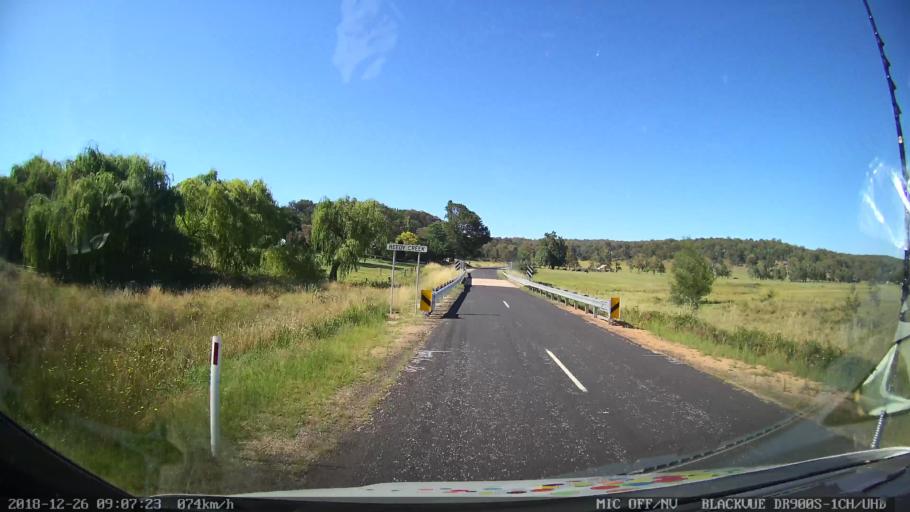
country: AU
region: New South Wales
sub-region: Mid-Western Regional
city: Kandos
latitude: -32.7049
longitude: 150.0045
